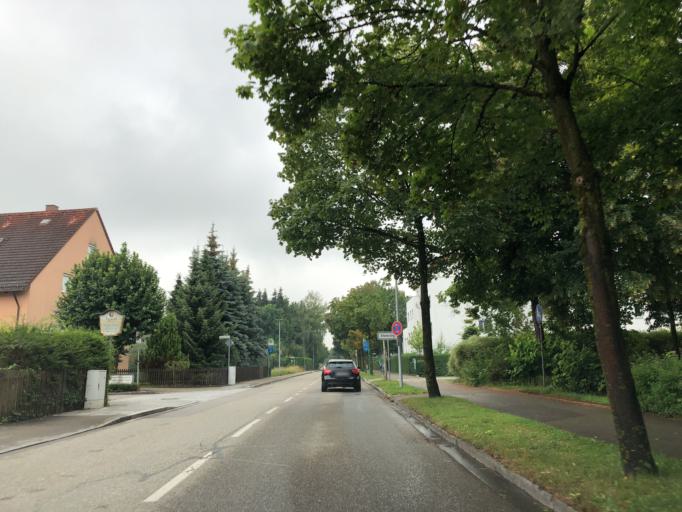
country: DE
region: Bavaria
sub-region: Upper Bavaria
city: Erding
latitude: 48.3003
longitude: 11.9091
